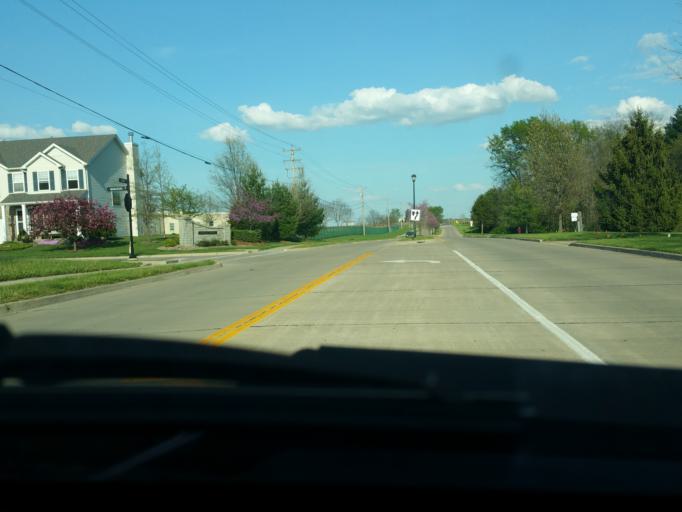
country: US
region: Illinois
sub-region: Madison County
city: Edwardsville
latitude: 38.7813
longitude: -89.9295
